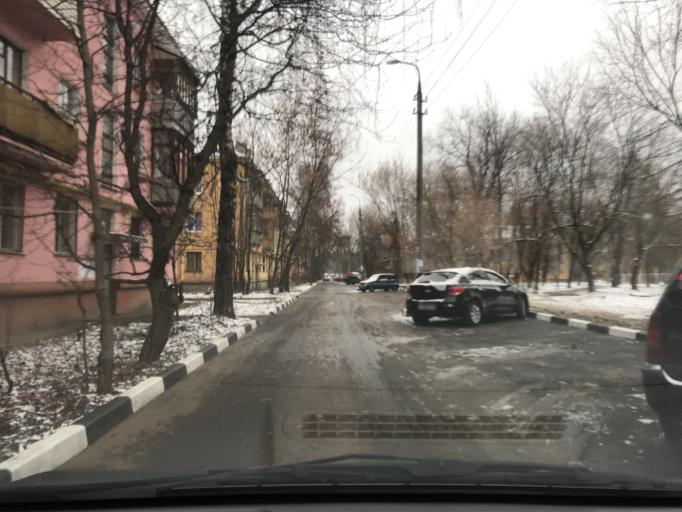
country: RU
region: Moskovskaya
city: Elektrostal'
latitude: 55.8049
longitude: 38.4623
